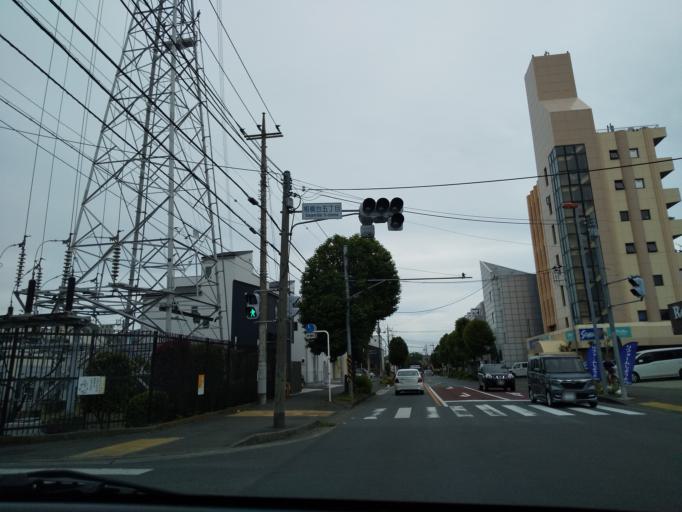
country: JP
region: Kanagawa
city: Zama
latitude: 35.5158
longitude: 139.4059
